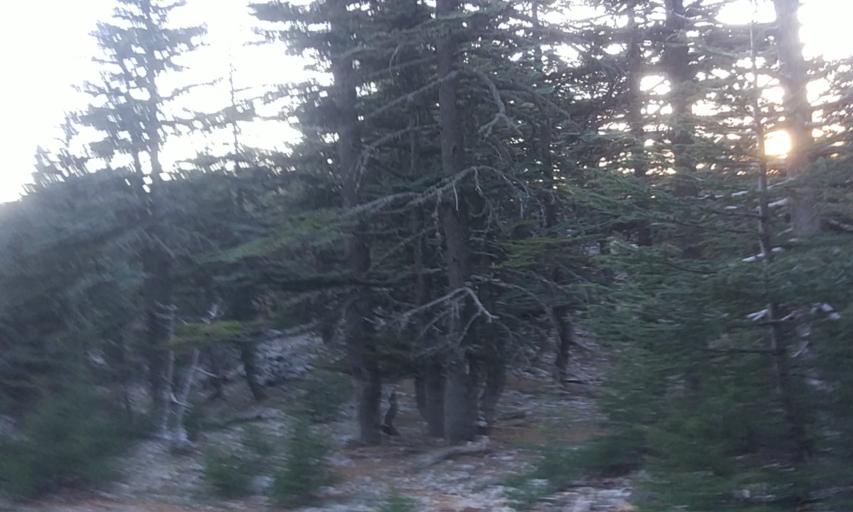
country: TR
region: Antalya
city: Altinyaka
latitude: 36.5383
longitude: 30.4170
